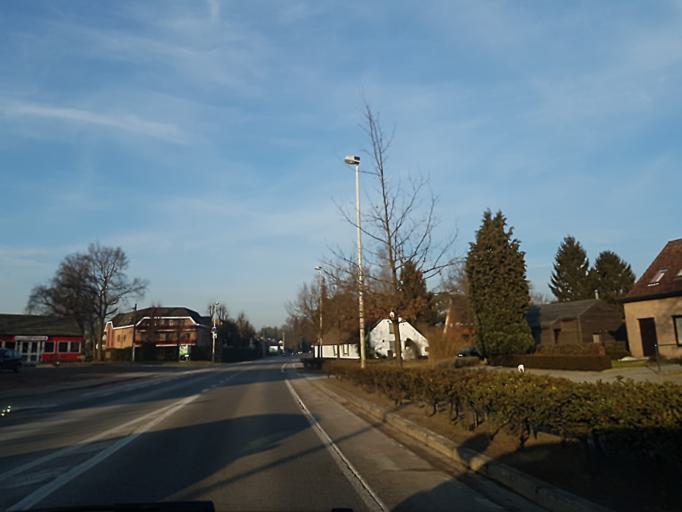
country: BE
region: Flanders
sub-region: Provincie Antwerpen
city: Zoersel
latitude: 51.2728
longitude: 4.7152
